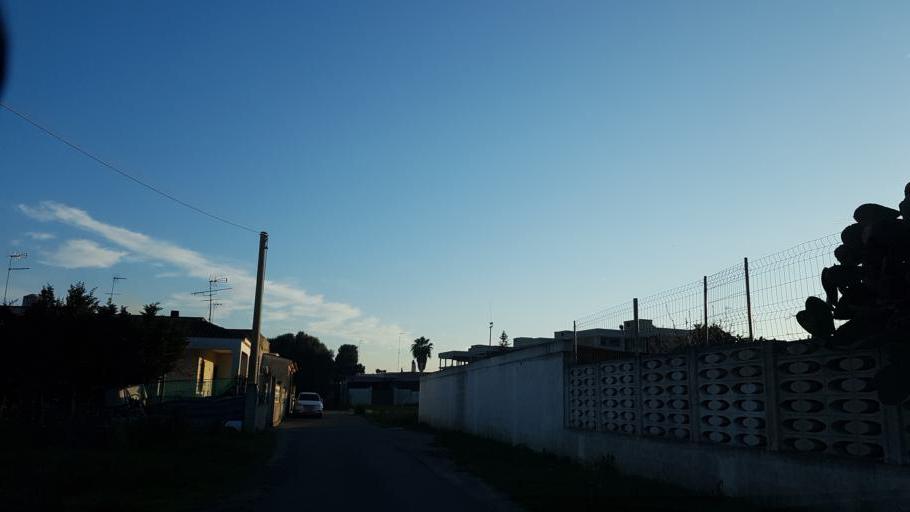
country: IT
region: Apulia
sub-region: Provincia di Brindisi
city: Tuturano
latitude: 40.5442
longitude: 17.9529
